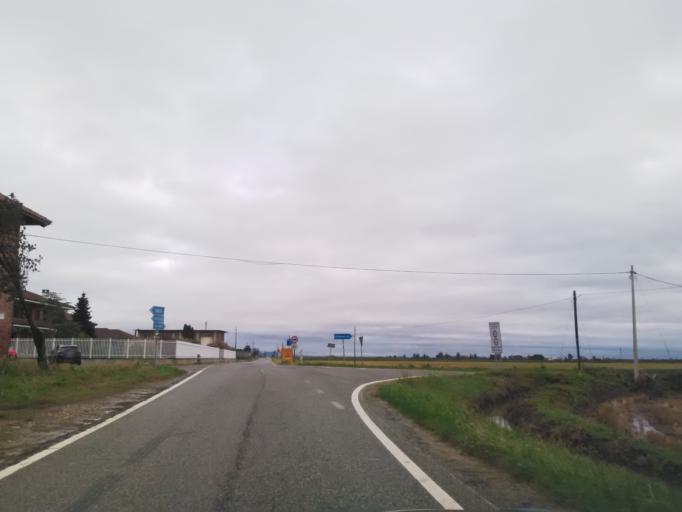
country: IT
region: Piedmont
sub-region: Provincia di Vercelli
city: Carisio
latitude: 45.4080
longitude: 8.2461
